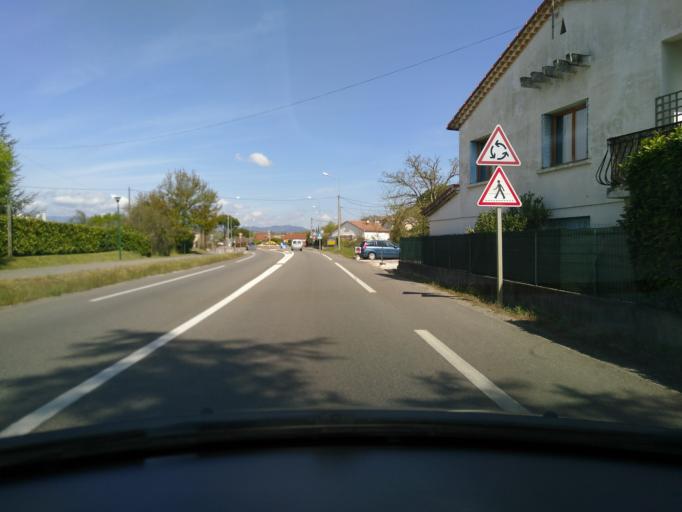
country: FR
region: Rhone-Alpes
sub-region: Departement de l'Ardeche
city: Ruoms
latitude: 44.4489
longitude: 4.3486
